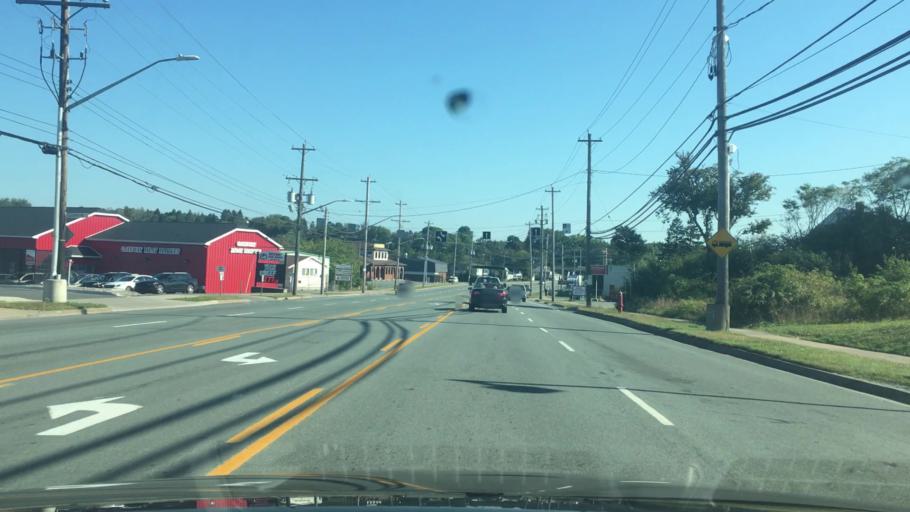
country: CA
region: Nova Scotia
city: Cole Harbour
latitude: 44.6954
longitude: -63.4968
